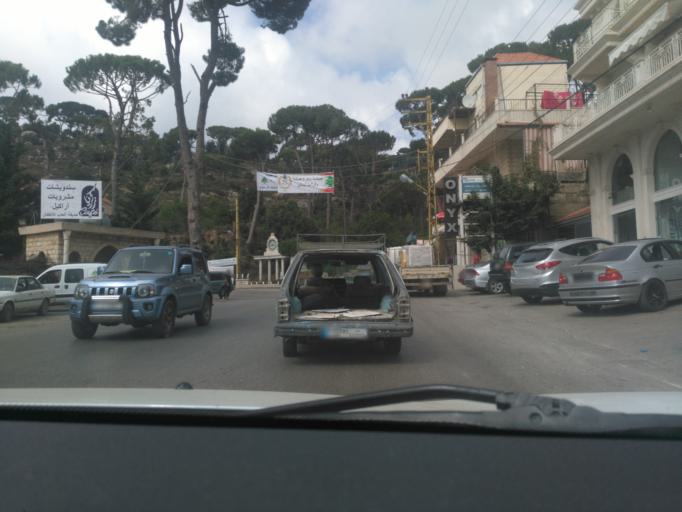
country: LB
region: Mont-Liban
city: Bhamdoun el Mhatta
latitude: 33.8489
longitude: 35.7277
